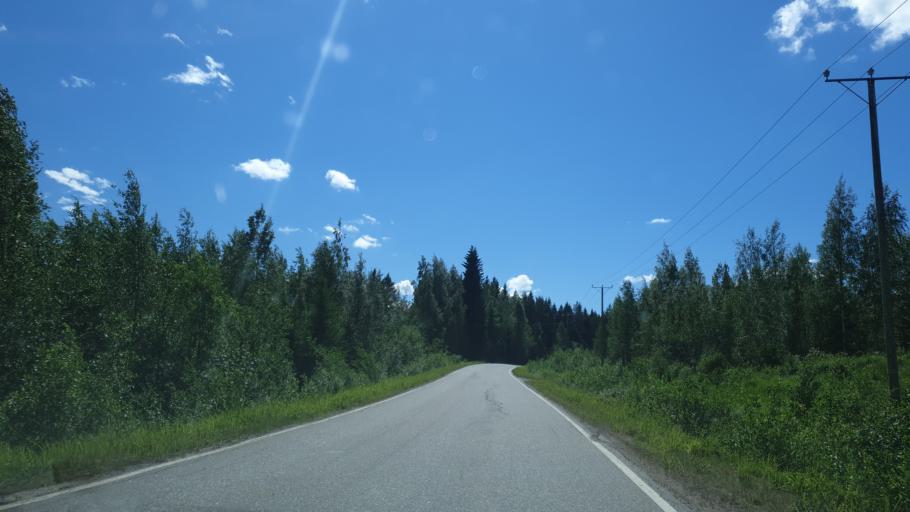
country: FI
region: Northern Savo
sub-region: Koillis-Savo
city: Kaavi
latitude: 63.0404
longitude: 28.5750
